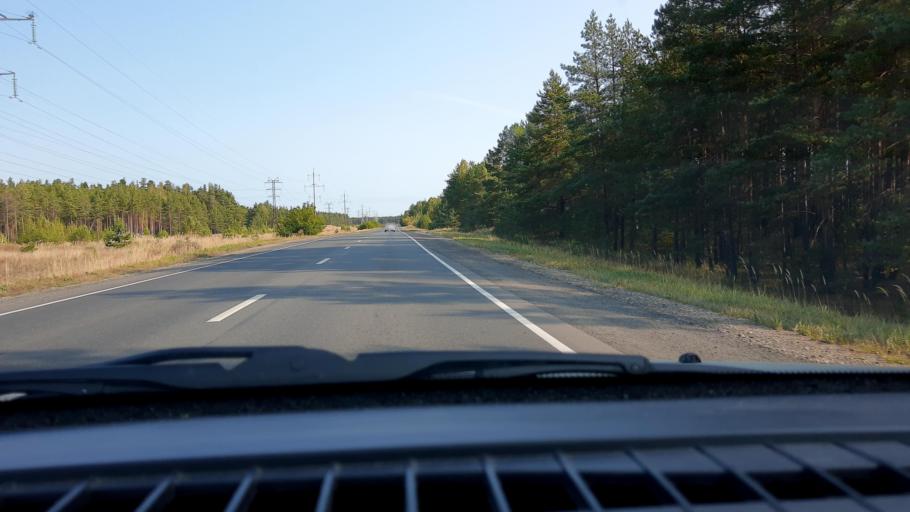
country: RU
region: Nizjnij Novgorod
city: Lukino
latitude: 56.3904
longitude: 43.6416
